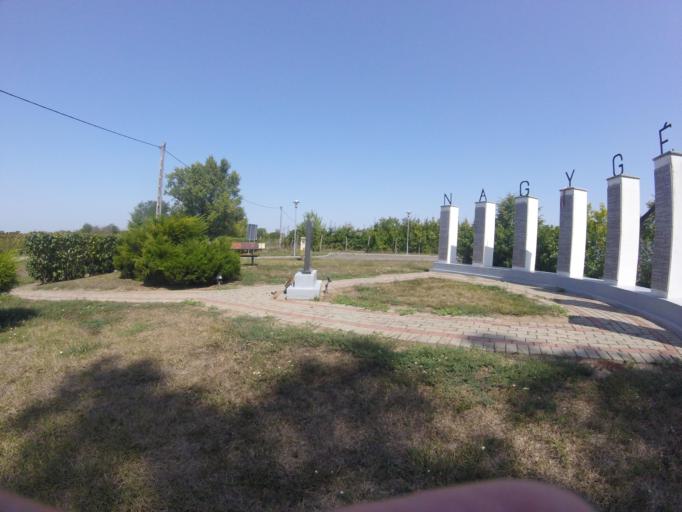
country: RO
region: Satu Mare
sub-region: Comuna Dorolt
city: Dara
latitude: 47.8484
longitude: 22.7442
